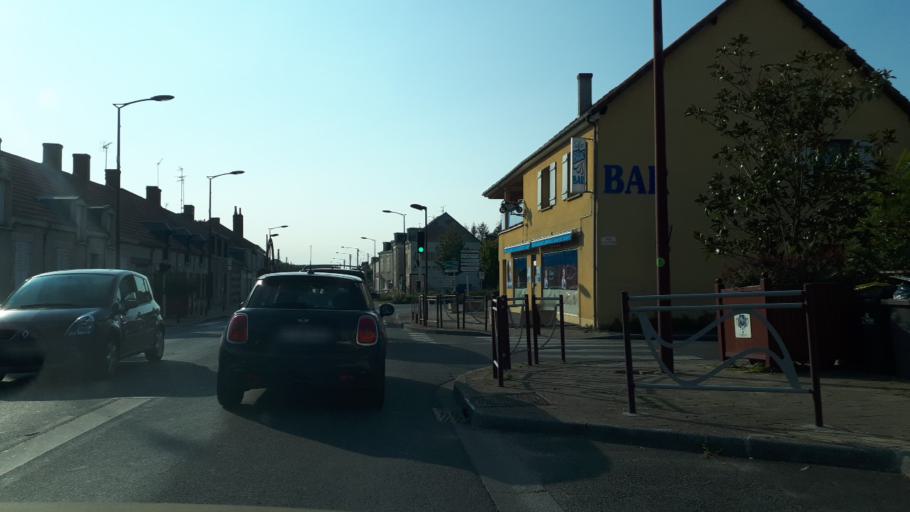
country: FR
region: Centre
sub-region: Departement du Cher
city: Vierzon
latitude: 47.2177
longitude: 2.0992
